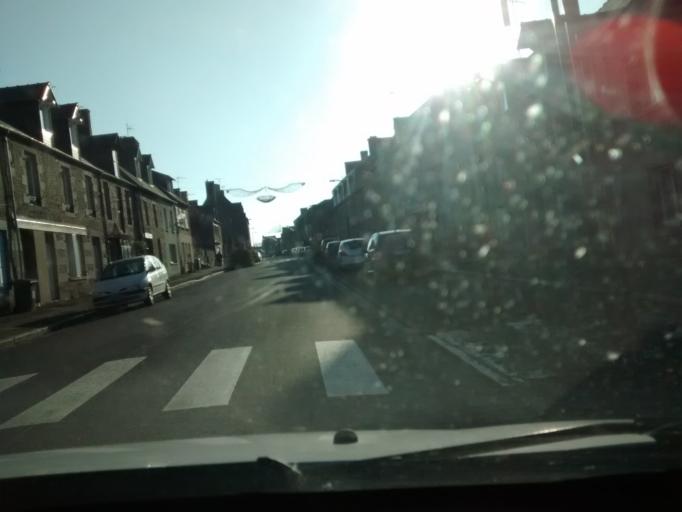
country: FR
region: Lower Normandy
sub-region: Departement de la Manche
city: Pontorson
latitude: 48.5559
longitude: -1.5093
